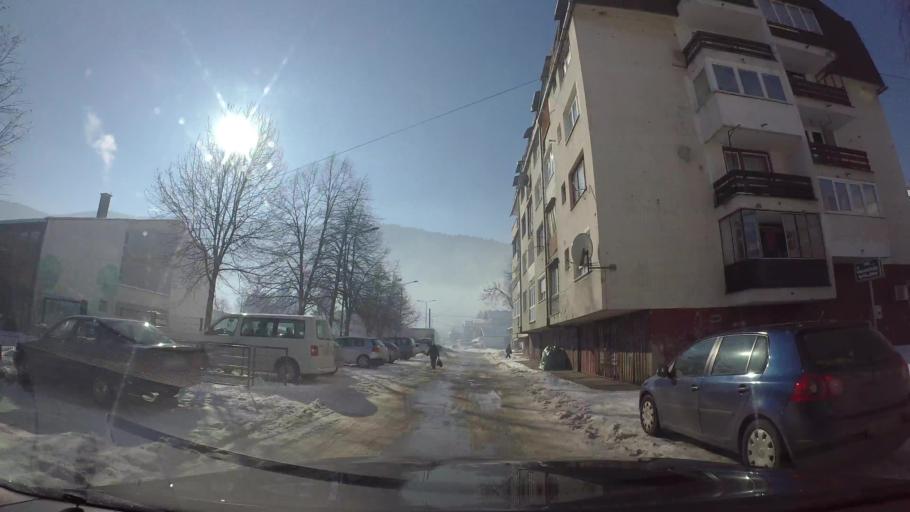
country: BA
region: Federation of Bosnia and Herzegovina
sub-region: Kanton Sarajevo
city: Sarajevo
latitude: 43.7951
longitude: 18.3210
